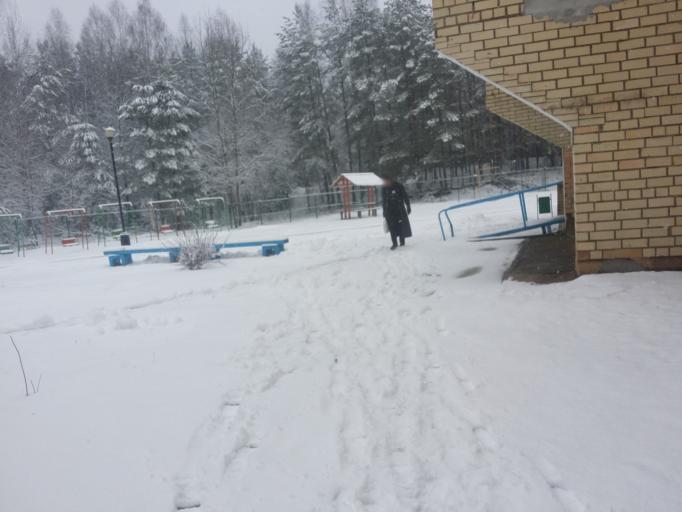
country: BY
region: Minsk
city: Rakaw
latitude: 53.9716
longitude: 27.0141
